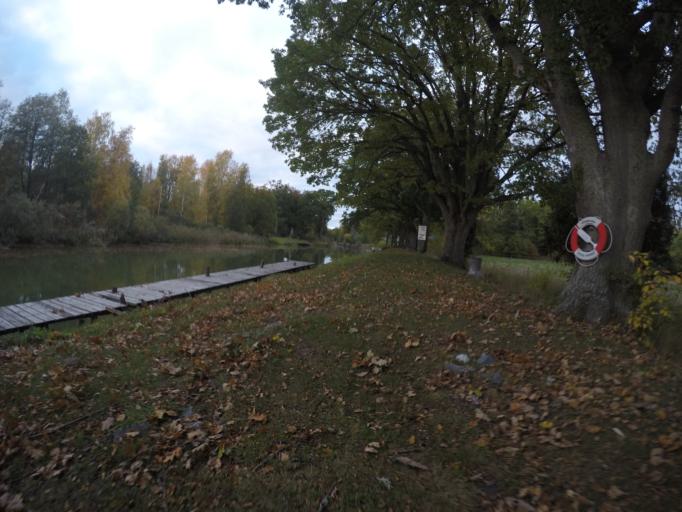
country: SE
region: Vaestmanland
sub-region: Arboga Kommun
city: Tyringe
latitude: 59.2926
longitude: 16.0029
